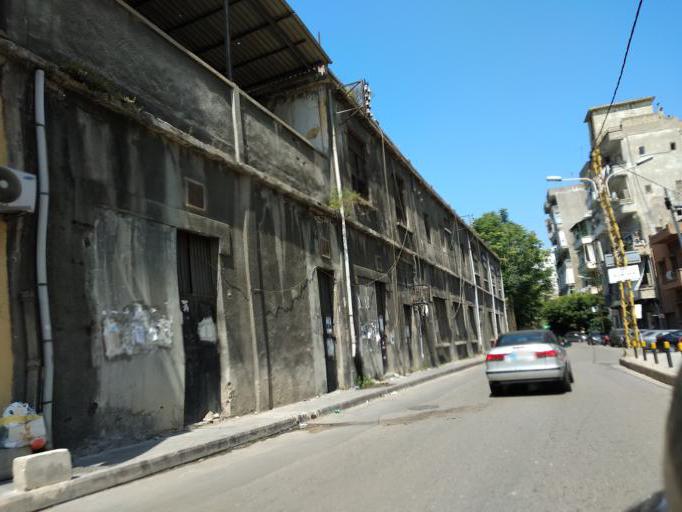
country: LB
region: Mont-Liban
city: Jdaidet el Matn
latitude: 33.8952
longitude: 35.5315
